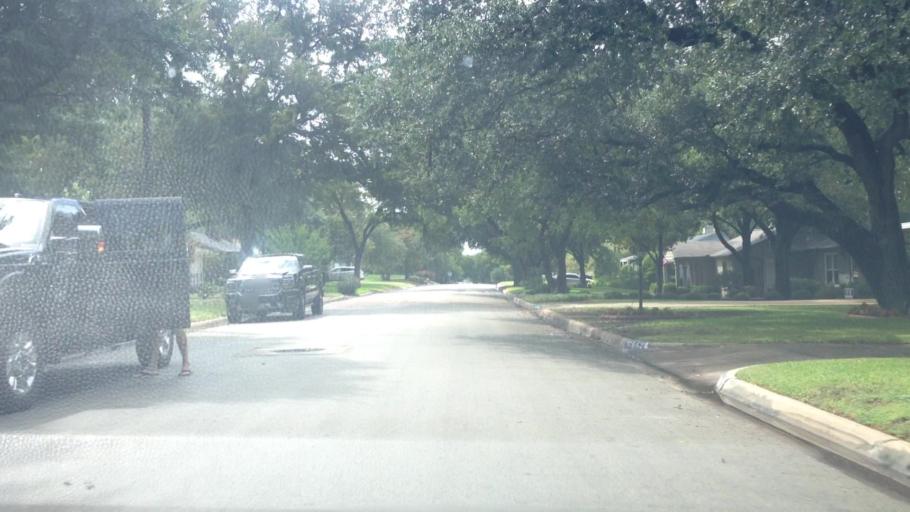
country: US
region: Texas
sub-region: Tarrant County
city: Westworth
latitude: 32.7334
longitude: -97.4256
